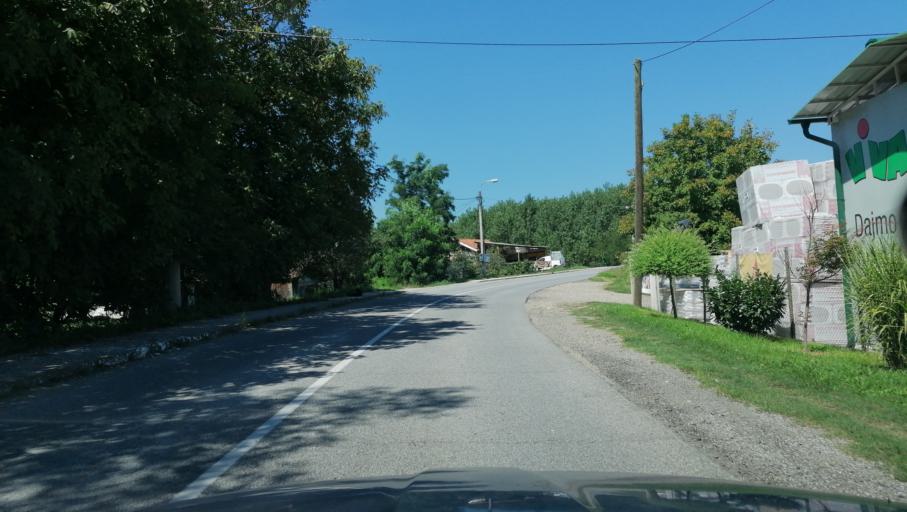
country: RS
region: Central Serbia
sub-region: Raski Okrug
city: Kraljevo
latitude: 43.6926
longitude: 20.5966
